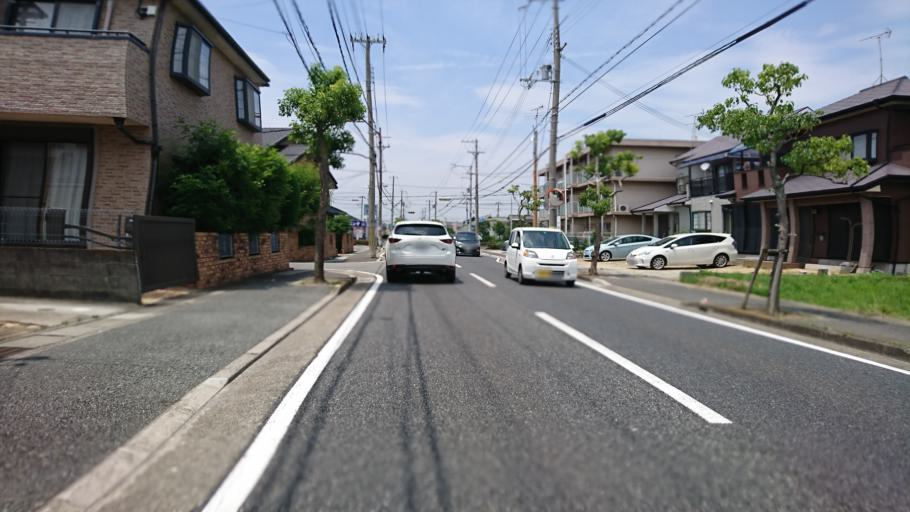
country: JP
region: Hyogo
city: Kakogawacho-honmachi
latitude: 34.7177
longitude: 134.8831
